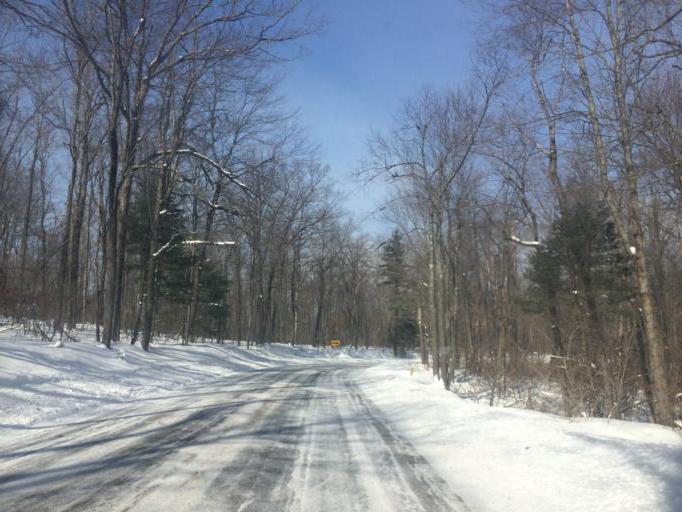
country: US
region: Pennsylvania
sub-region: Centre County
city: Stormstown
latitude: 40.8873
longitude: -78.0289
